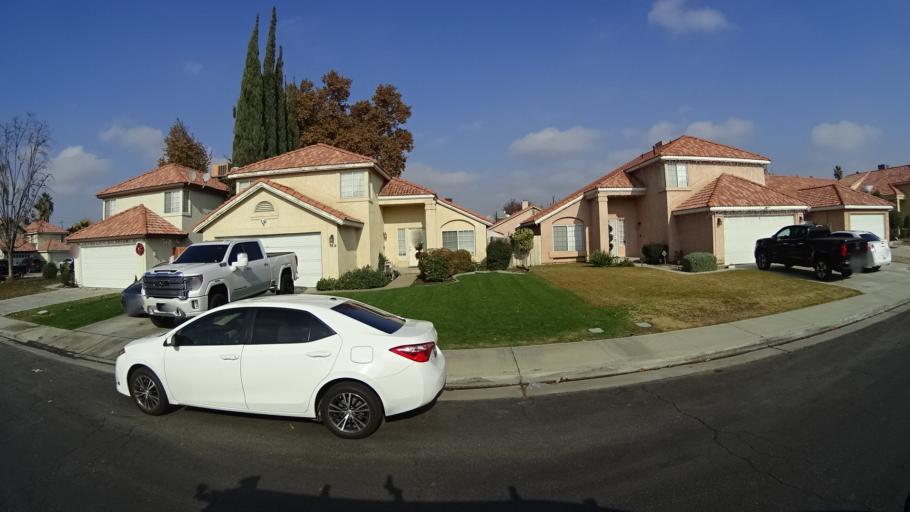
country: US
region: California
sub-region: Kern County
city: Greenacres
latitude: 35.3020
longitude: -119.0907
